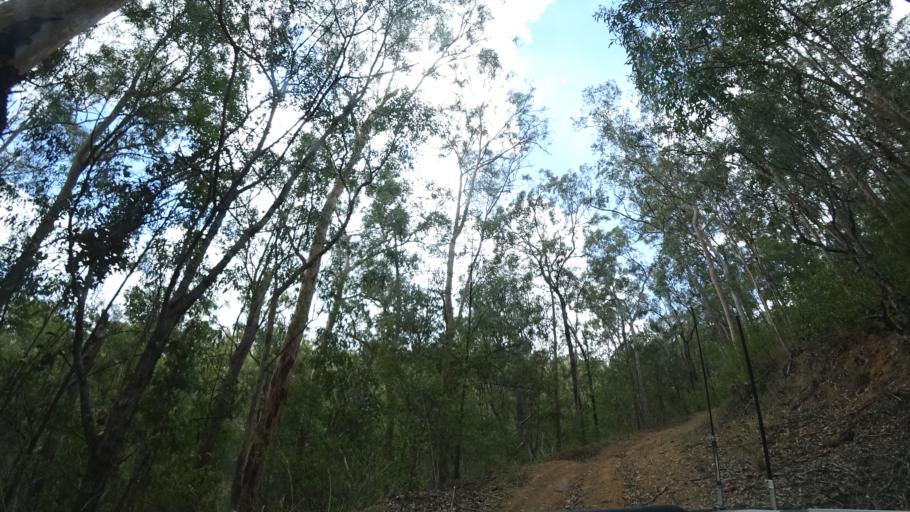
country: AU
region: Queensland
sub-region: Moreton Bay
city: Highvale
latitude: -27.4072
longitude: 152.7398
